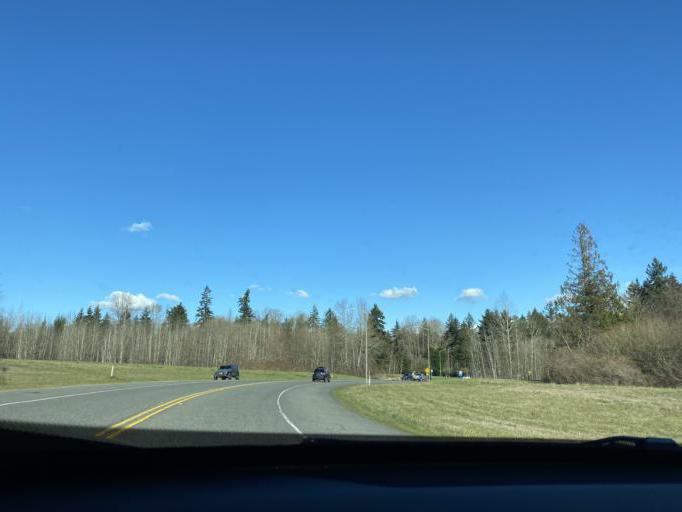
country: US
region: Washington
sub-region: King County
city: Federal Way
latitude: 47.3023
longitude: -122.2998
